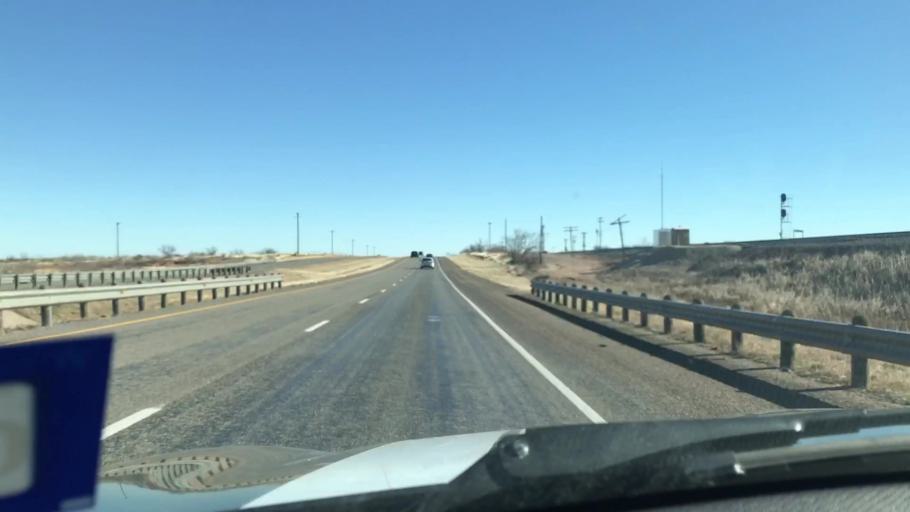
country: US
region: Texas
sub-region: Garza County
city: Post
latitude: 33.1361
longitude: -101.3096
